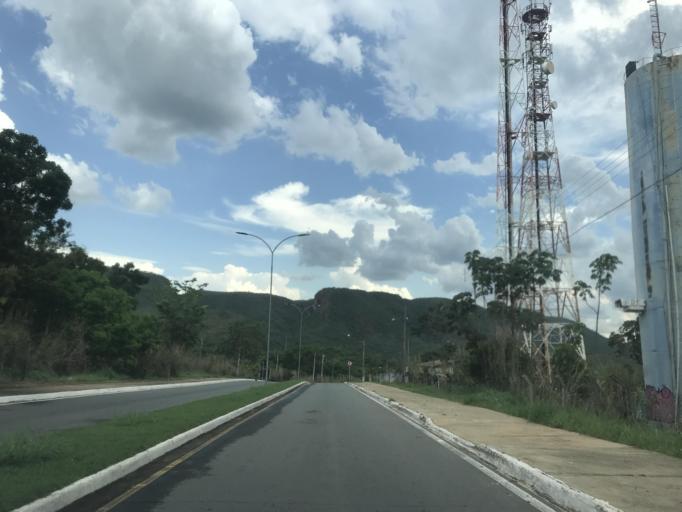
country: BR
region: Goias
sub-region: Caldas Novas
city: Caldas Novas
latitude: -17.7668
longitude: -48.7556
